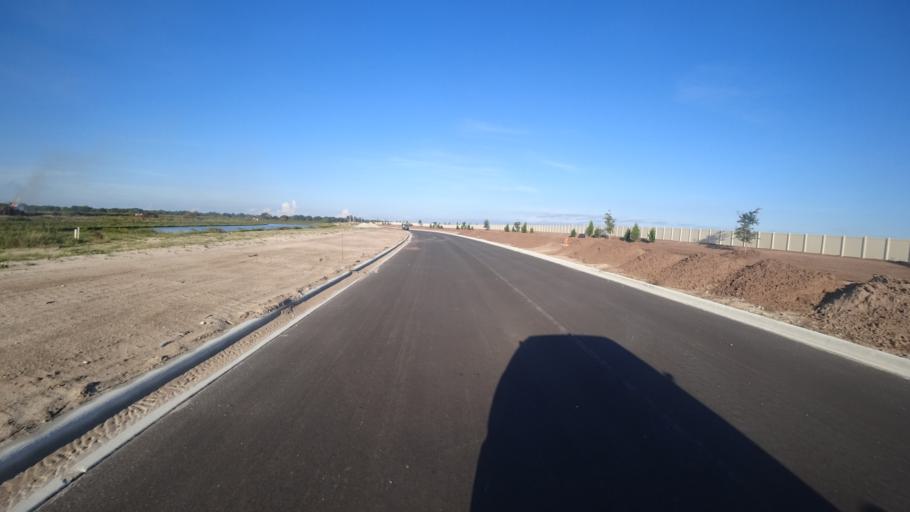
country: US
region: Florida
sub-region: Sarasota County
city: The Meadows
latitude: 27.4544
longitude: -82.3845
